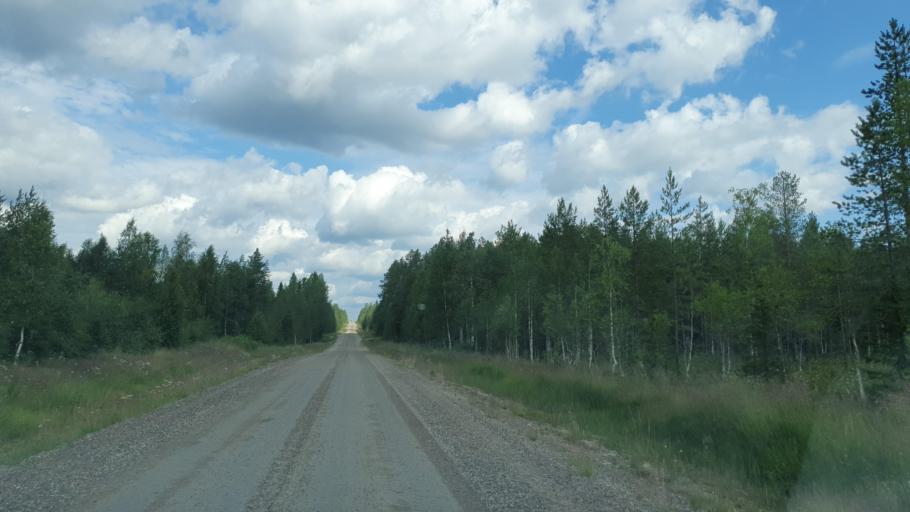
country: FI
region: Kainuu
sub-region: Kehys-Kainuu
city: Kuhmo
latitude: 64.4693
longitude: 29.5973
